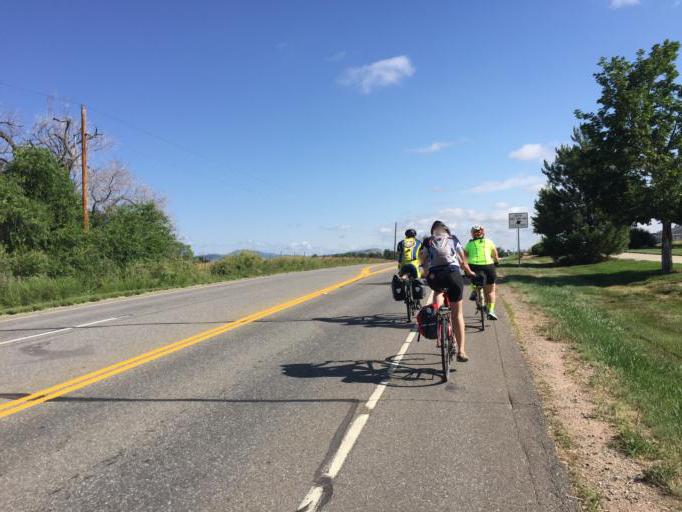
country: US
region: Colorado
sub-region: Boulder County
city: Niwot
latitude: 40.1446
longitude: -105.1781
